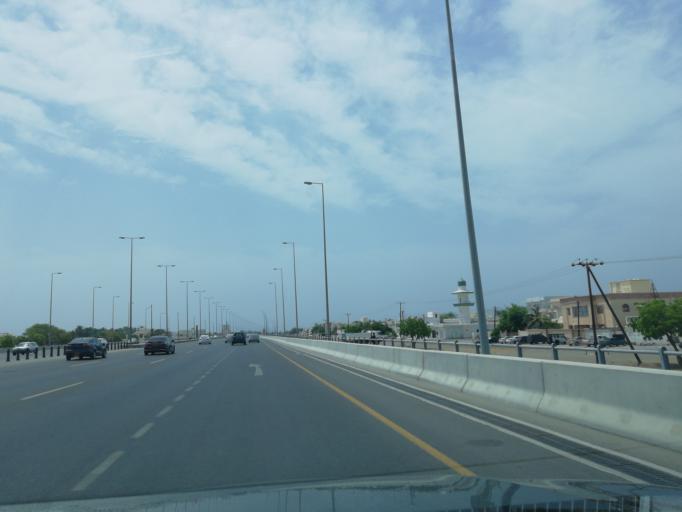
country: OM
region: Muhafazat Masqat
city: As Sib al Jadidah
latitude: 23.6670
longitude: 58.1566
